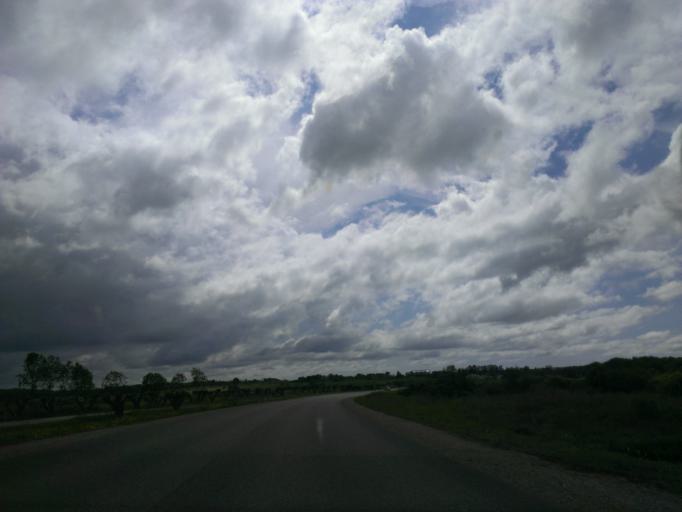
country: LV
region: Durbe
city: Liegi
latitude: 56.5882
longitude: 21.3591
